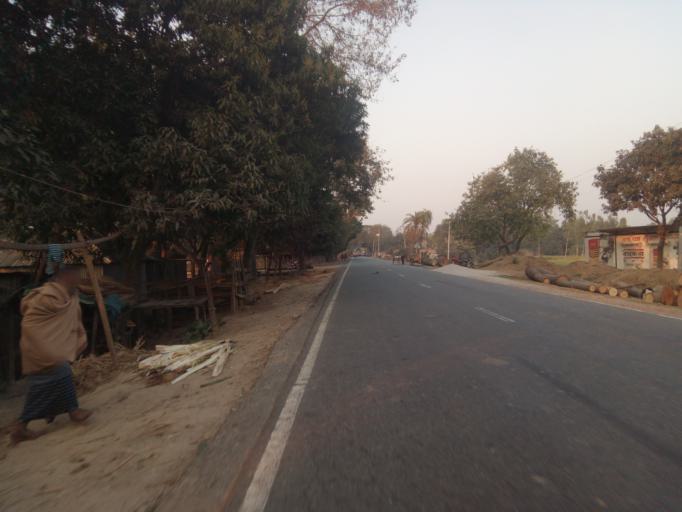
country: BD
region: Rajshahi
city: Bogra
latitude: 24.6254
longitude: 89.2425
